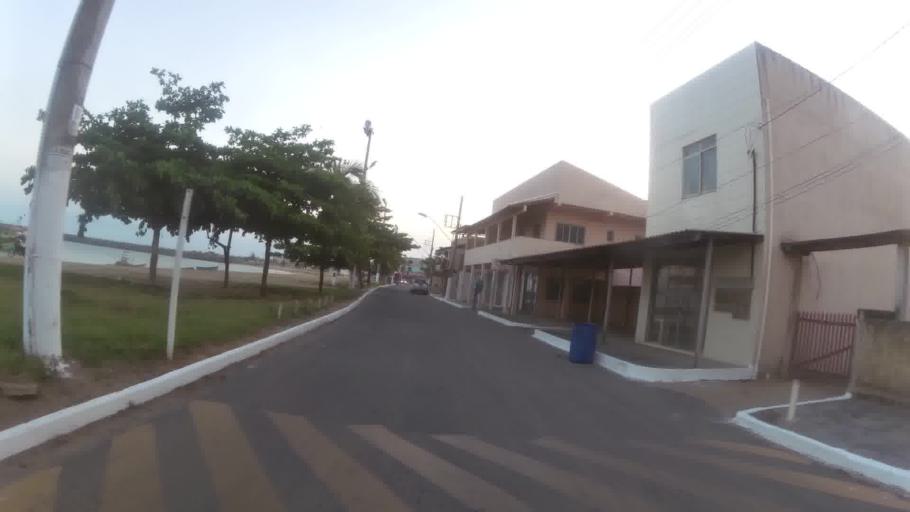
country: BR
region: Espirito Santo
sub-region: Piuma
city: Piuma
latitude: -20.8913
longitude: -40.7719
